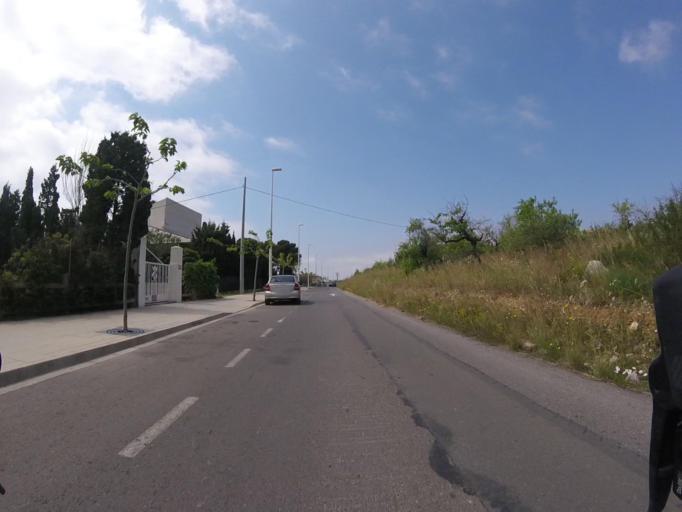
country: ES
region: Valencia
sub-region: Provincia de Castello
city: Alcoceber
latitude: 40.2493
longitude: 0.2765
